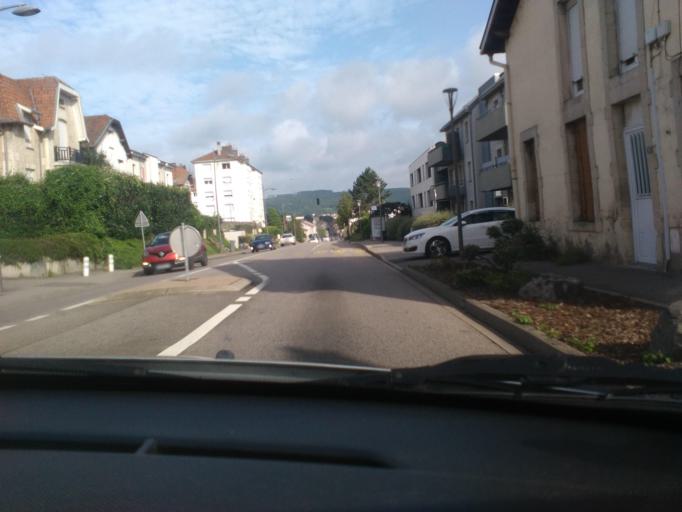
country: FR
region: Lorraine
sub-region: Departement de Meurthe-et-Moselle
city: Frouard
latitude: 48.7532
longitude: 6.1438
